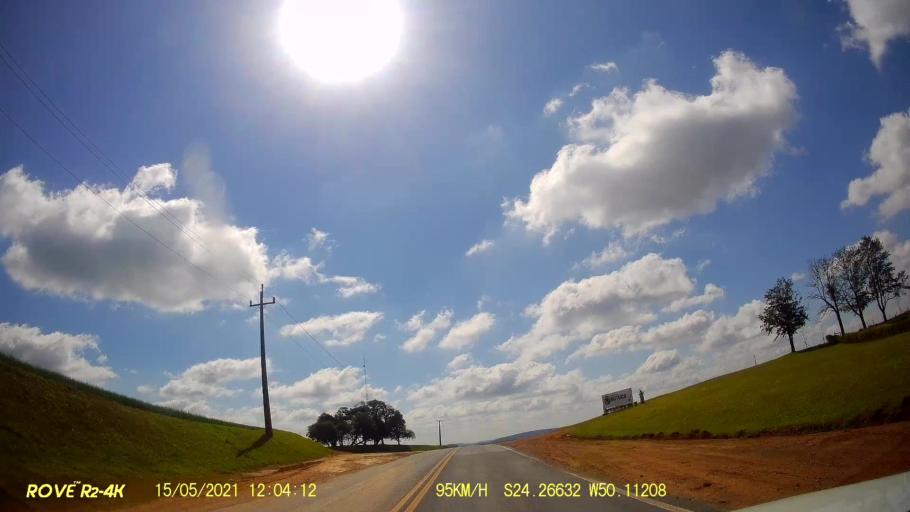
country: BR
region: Parana
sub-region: Pirai Do Sul
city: Pirai do Sul
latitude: -24.2665
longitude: -50.1120
